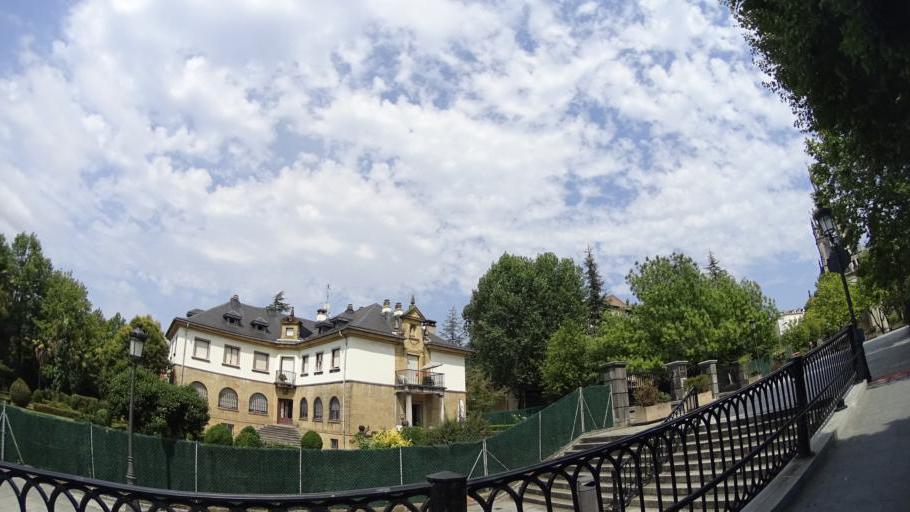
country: ES
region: Basque Country
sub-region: Bizkaia
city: Santutxu
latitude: 43.2591
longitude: -2.9157
